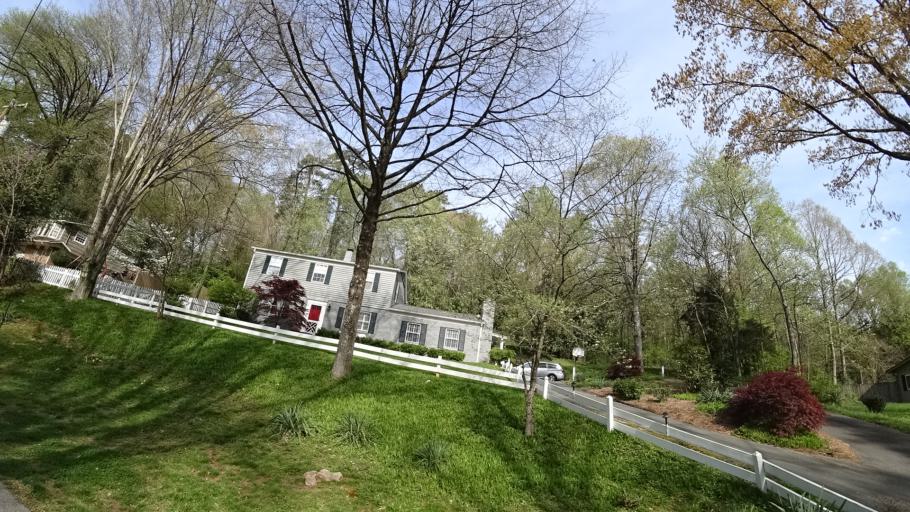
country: US
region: Tennessee
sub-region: Knox County
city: Knoxville
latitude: 35.9014
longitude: -83.9845
